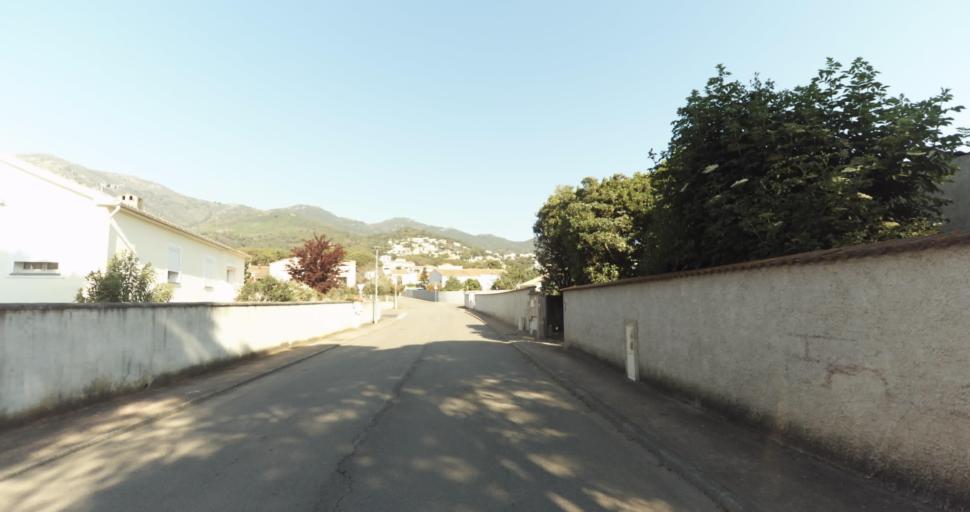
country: FR
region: Corsica
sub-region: Departement de la Haute-Corse
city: Biguglia
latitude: 42.6367
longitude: 9.4327
